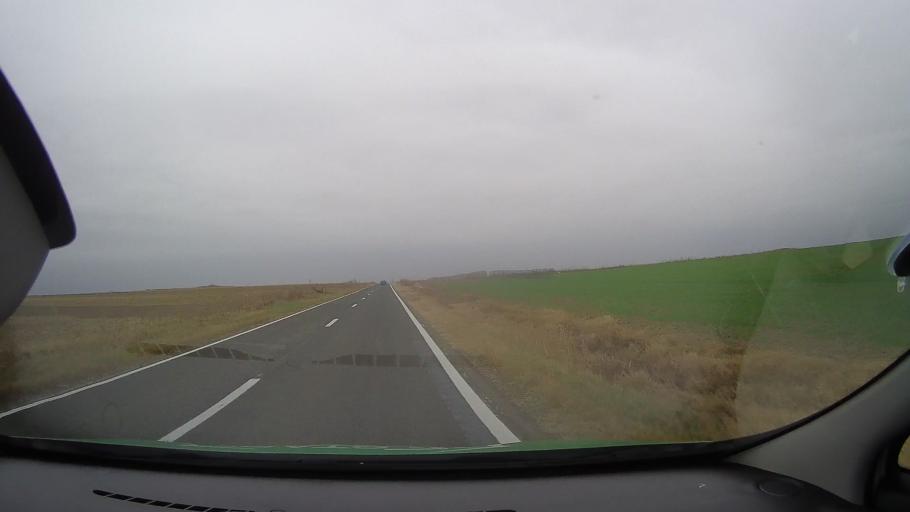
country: RO
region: Constanta
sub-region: Comuna Ciobanu
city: Ciobanu
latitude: 44.7028
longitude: 28.0282
